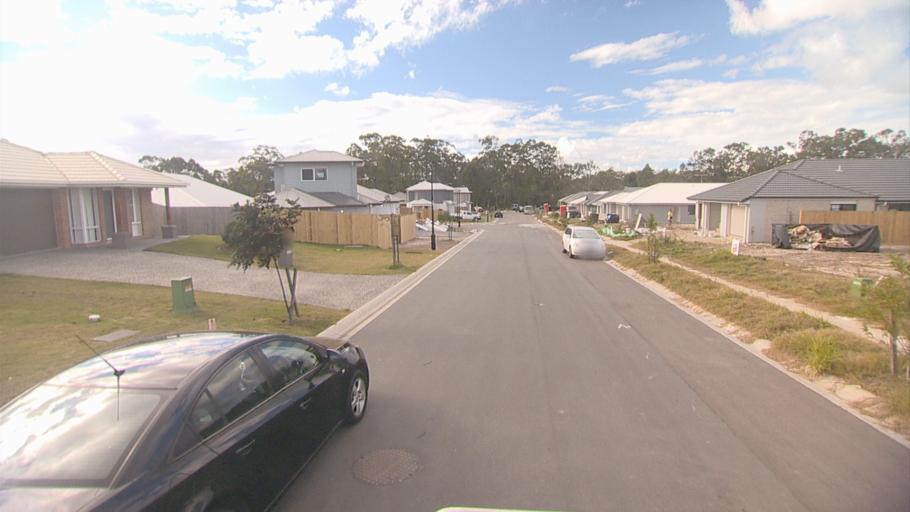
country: AU
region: Queensland
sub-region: Logan
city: Logan Reserve
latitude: -27.6941
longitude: 153.0966
